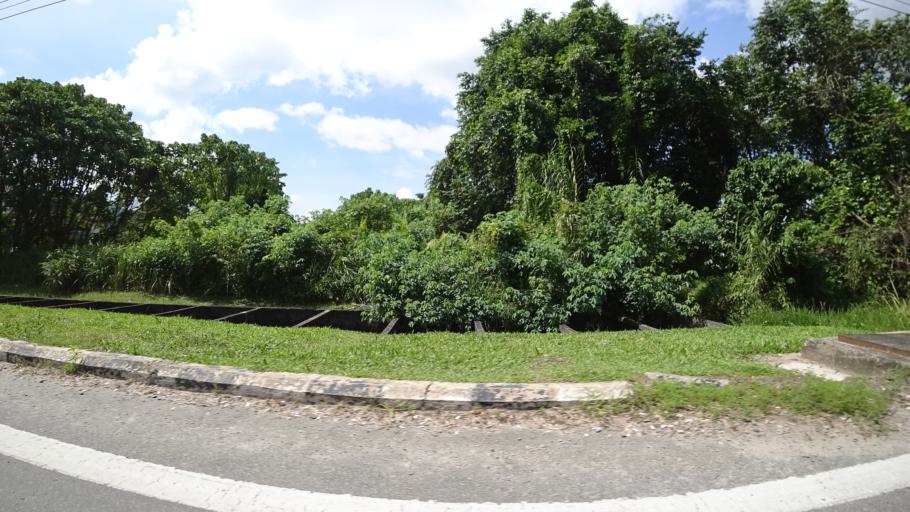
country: MY
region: Sarawak
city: Limbang
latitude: 4.7589
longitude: 115.0060
